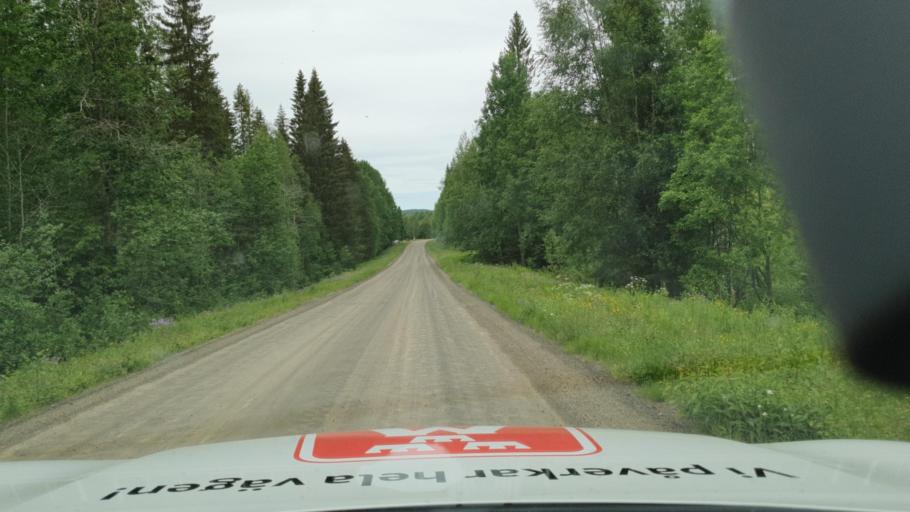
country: SE
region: Vaesterbotten
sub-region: Skelleftea Kommun
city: Burtraesk
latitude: 64.3310
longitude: 20.6204
